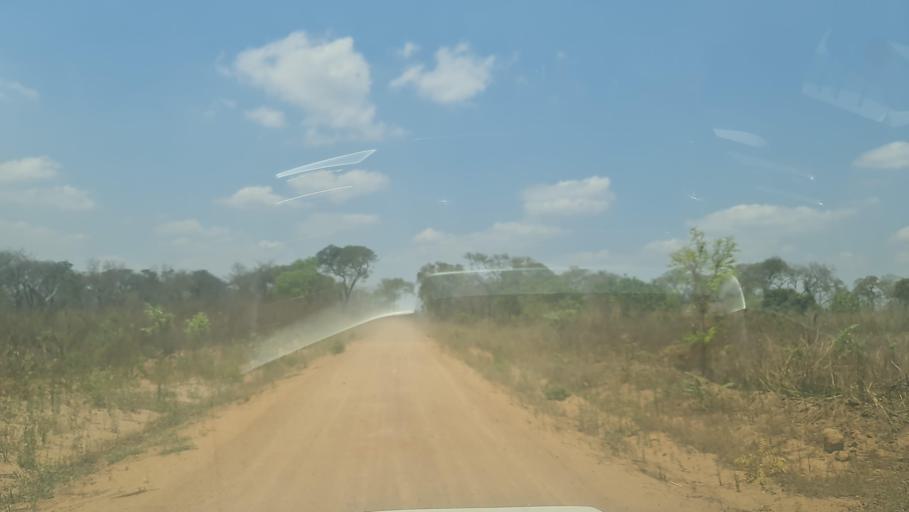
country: MW
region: Southern Region
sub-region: Nsanje District
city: Nsanje
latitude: -17.5584
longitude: 35.8980
